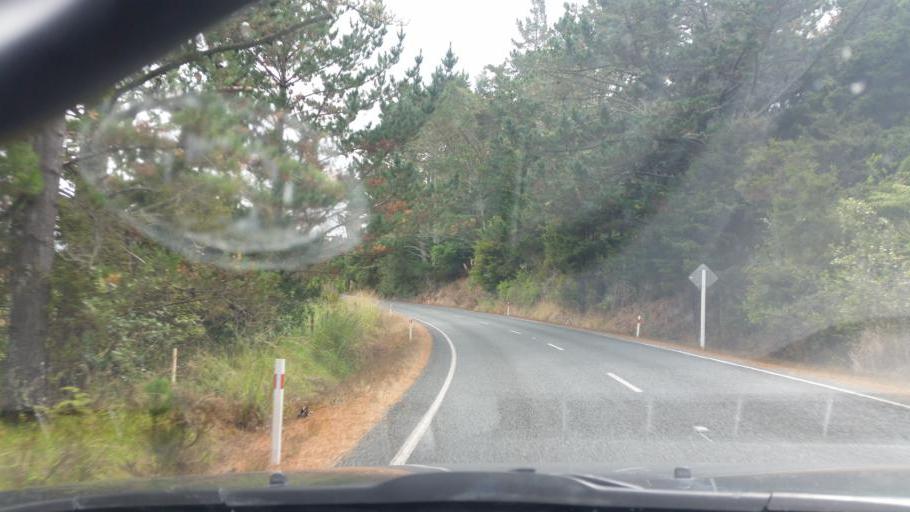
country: NZ
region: Northland
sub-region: Whangarei
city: Ruakaka
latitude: -35.9492
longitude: 174.2938
